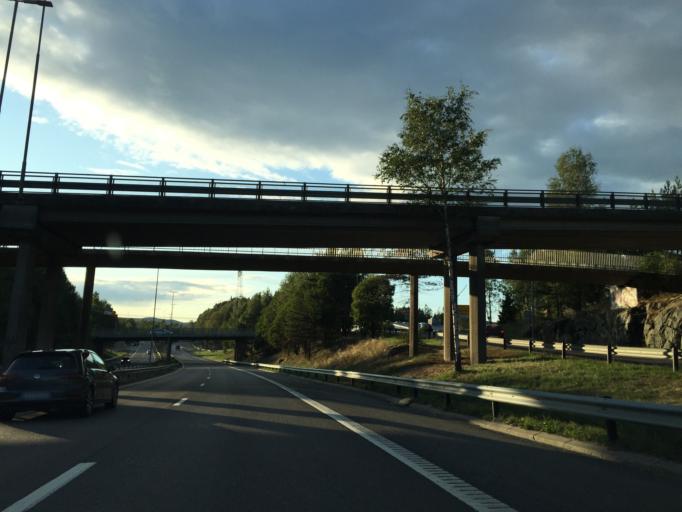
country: NO
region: Akershus
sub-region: Lorenskog
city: Kjenn
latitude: 59.9358
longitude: 10.9381
